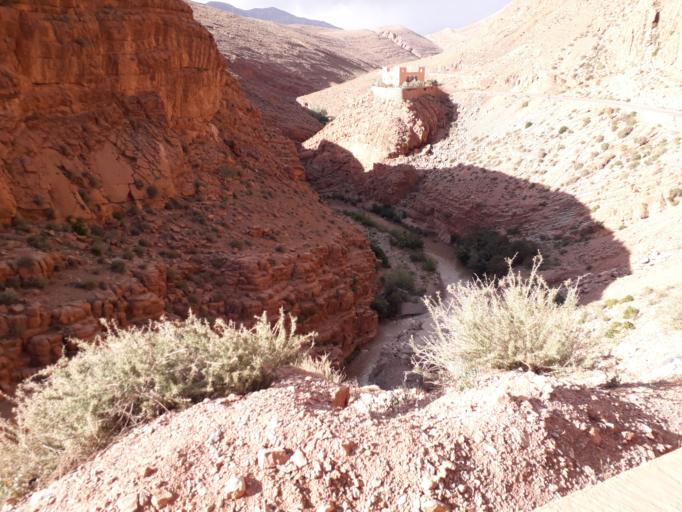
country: MA
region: Souss-Massa-Draa
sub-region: Ouarzazate
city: Imider
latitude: 31.5365
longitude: -5.9208
